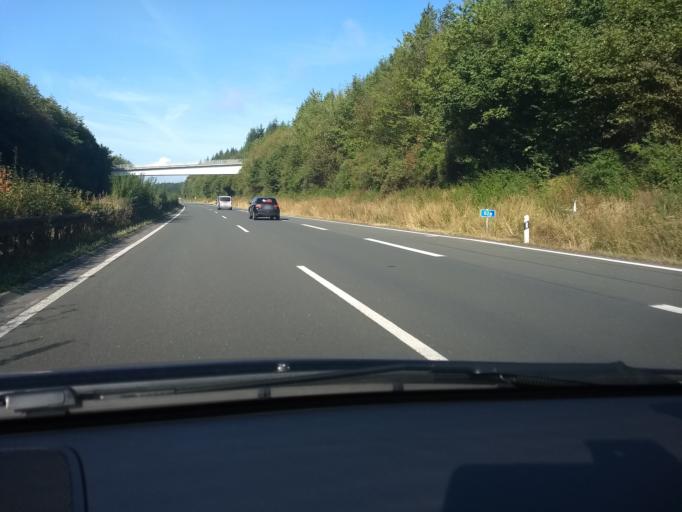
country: DE
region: North Rhine-Westphalia
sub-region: Regierungsbezirk Arnsberg
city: Meschede
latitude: 51.3649
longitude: 8.2871
